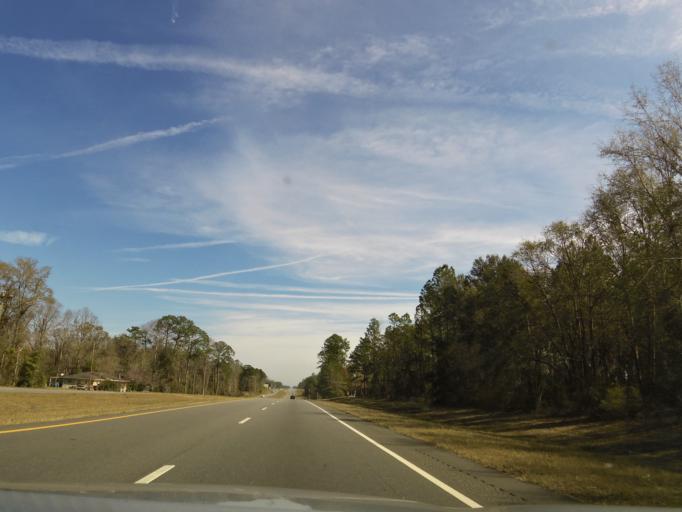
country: US
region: Georgia
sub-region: Brantley County
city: Nahunta
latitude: 31.2149
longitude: -81.8989
